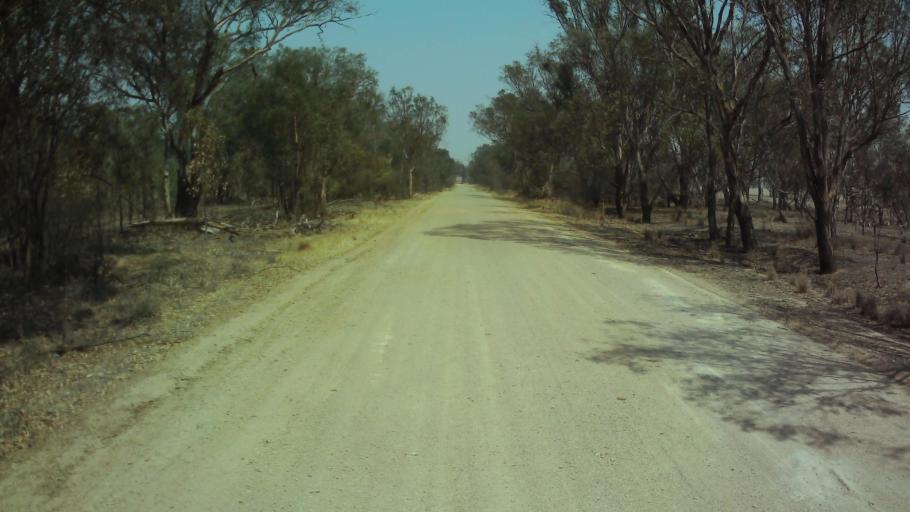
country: AU
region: New South Wales
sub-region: Weddin
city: Grenfell
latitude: -33.6455
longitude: 148.2651
